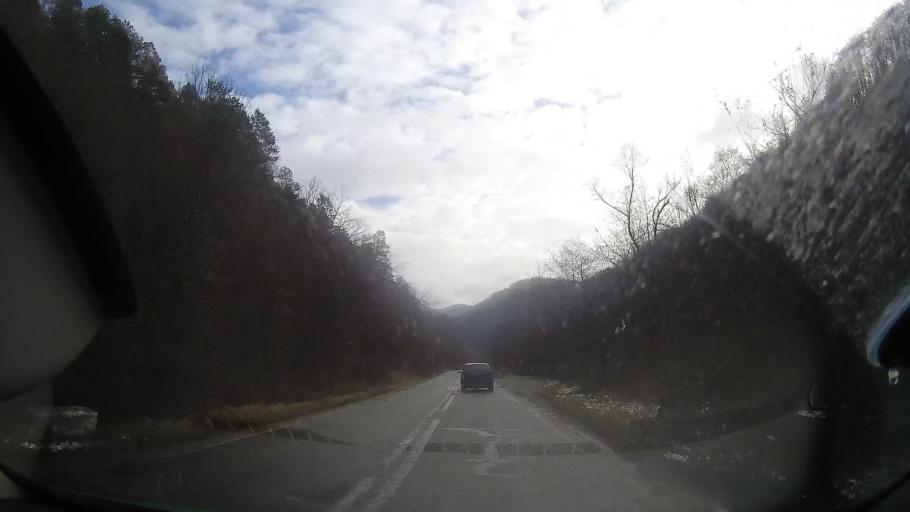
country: RO
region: Alba
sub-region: Oras Baia de Aries
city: Baia de Aries
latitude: 46.3827
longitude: 23.2613
